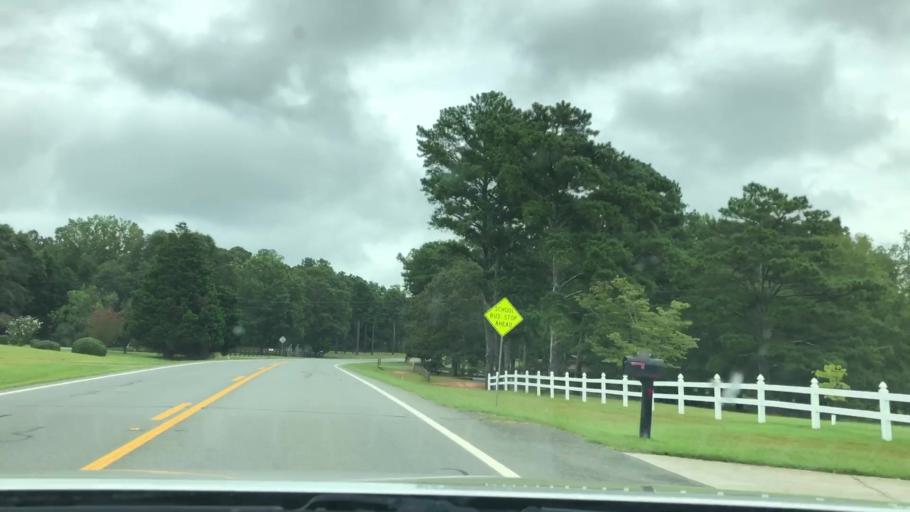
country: US
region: Georgia
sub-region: Pike County
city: Zebulon
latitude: 33.1108
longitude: -84.3980
